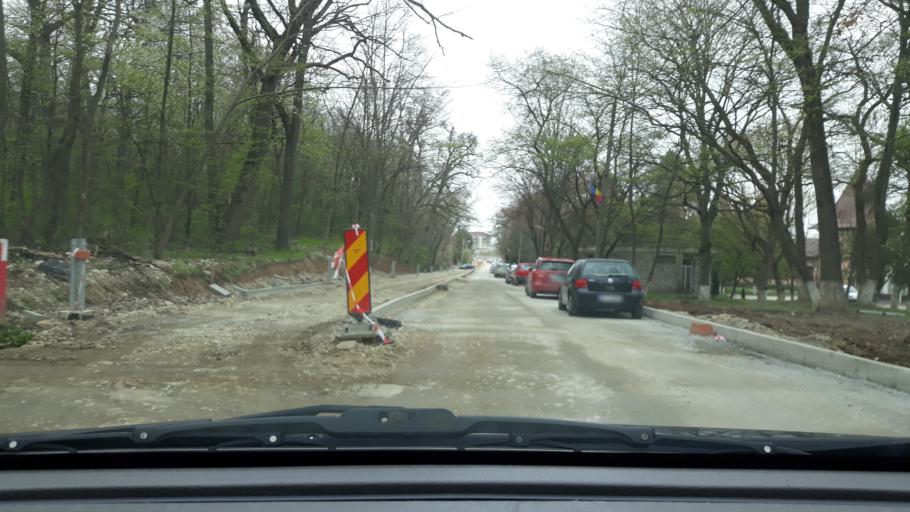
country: RO
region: Bihor
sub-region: Comuna Sanmartin
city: Sanmartin
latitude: 46.9933
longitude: 21.9773
